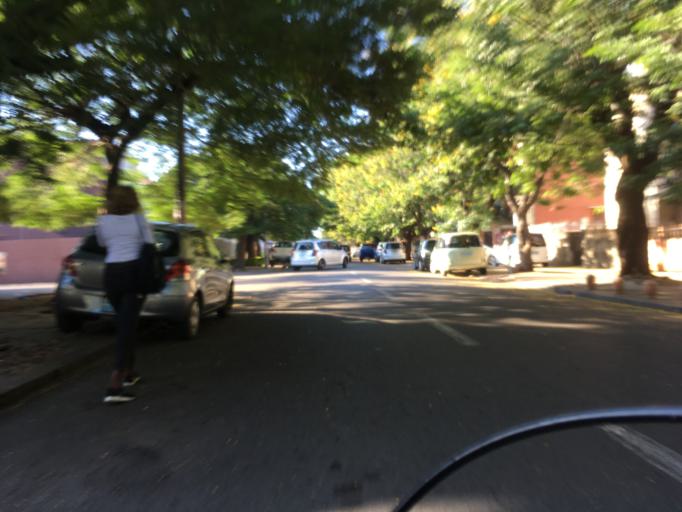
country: MZ
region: Maputo City
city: Maputo
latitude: -25.9620
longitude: 32.5807
